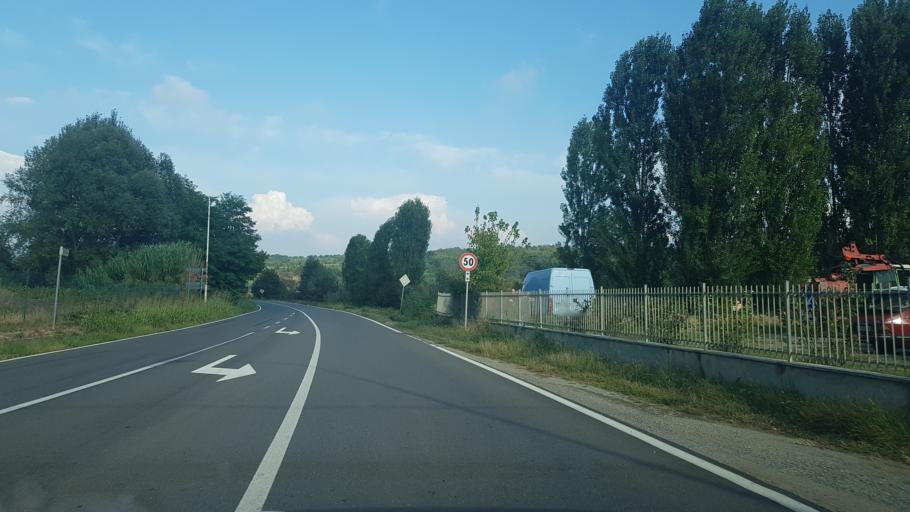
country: IT
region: Piedmont
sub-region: Provincia di Asti
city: Bruno
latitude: 44.7977
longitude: 8.4398
